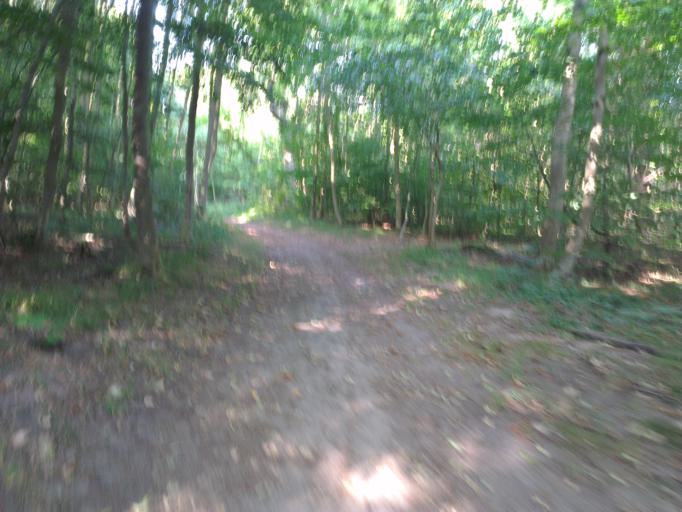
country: DK
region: Capital Region
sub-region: Frederikssund Kommune
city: Jaegerspris
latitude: 55.8587
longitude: 11.9838
